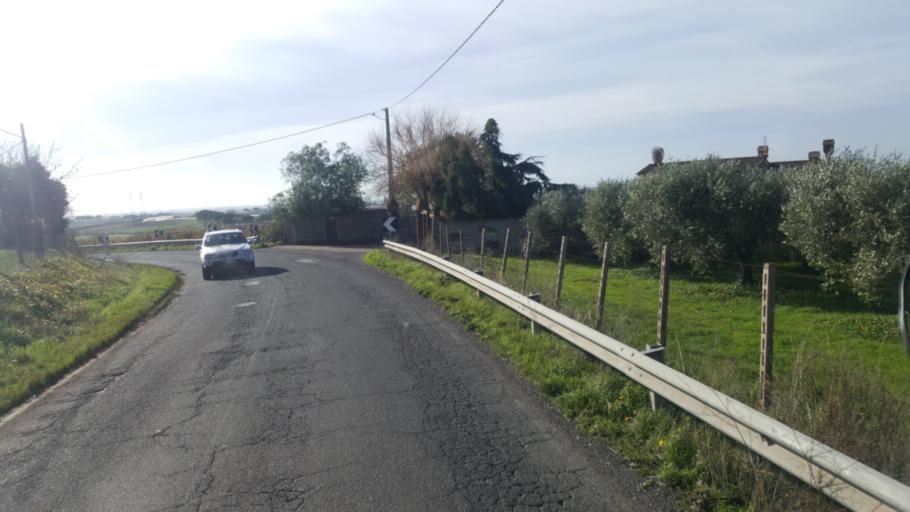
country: IT
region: Latium
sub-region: Citta metropolitana di Roma Capitale
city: Mantiglia di Ardea
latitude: 41.6639
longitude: 12.6302
